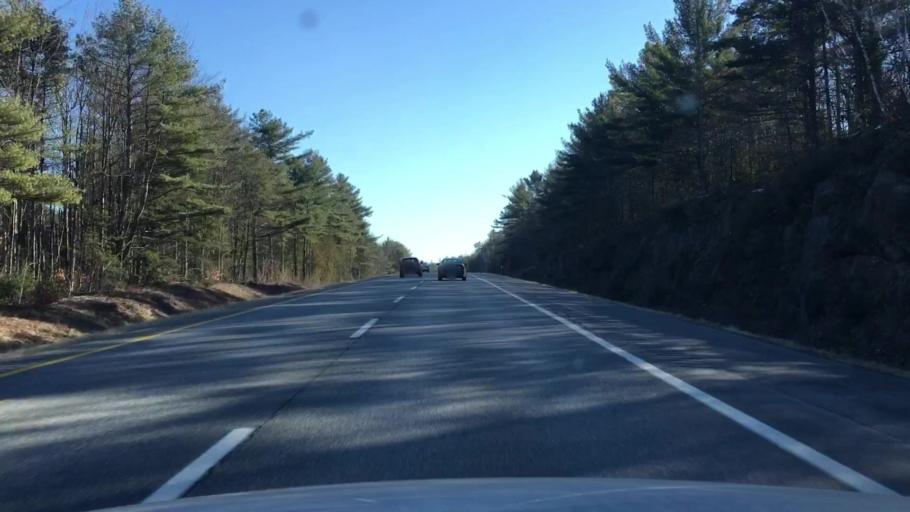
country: US
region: Maine
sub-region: Penobscot County
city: Plymouth
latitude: 44.7976
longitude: -69.2139
